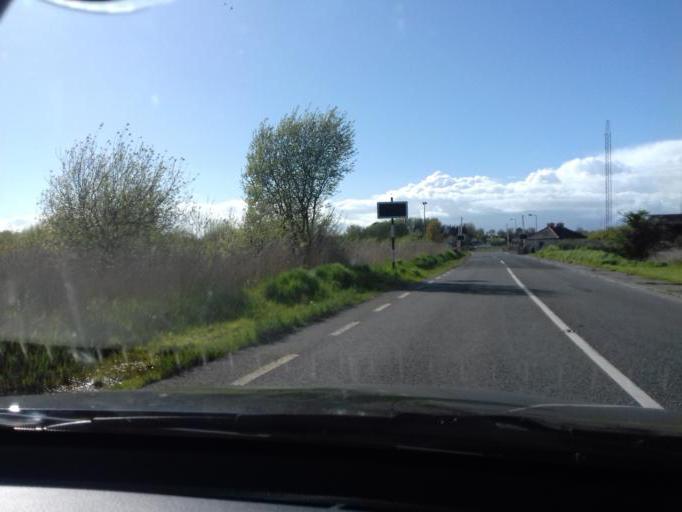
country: IE
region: Munster
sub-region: Waterford
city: Waterford
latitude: 52.2777
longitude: -7.1368
